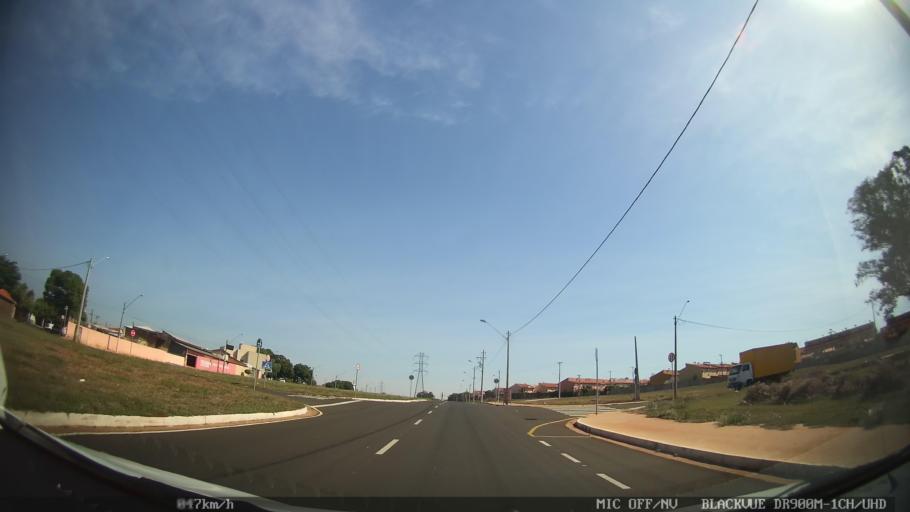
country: BR
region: Sao Paulo
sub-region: Sao Jose Do Rio Preto
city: Sao Jose do Rio Preto
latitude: -20.7895
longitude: -49.4181
